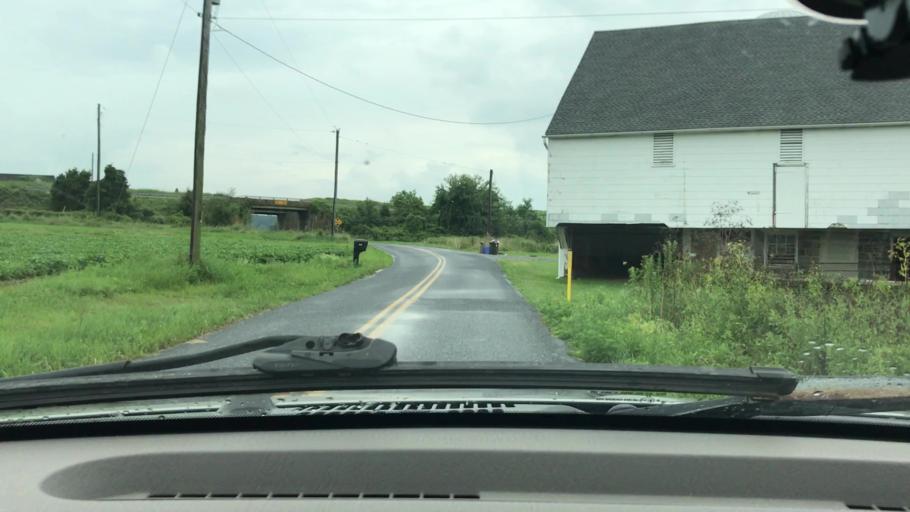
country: US
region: Pennsylvania
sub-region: Lancaster County
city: Elizabethtown
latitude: 40.1833
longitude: -76.6051
